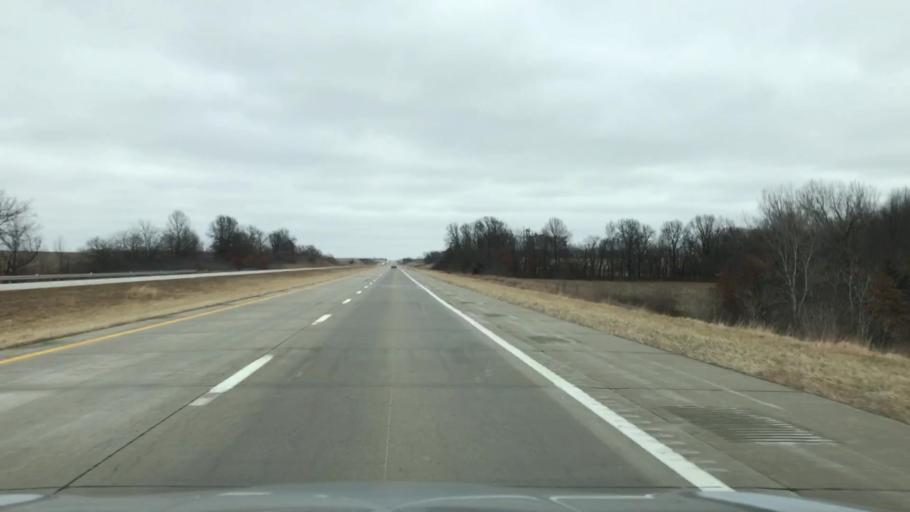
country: US
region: Missouri
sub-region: Caldwell County
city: Hamilton
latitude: 39.7354
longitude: -93.9204
